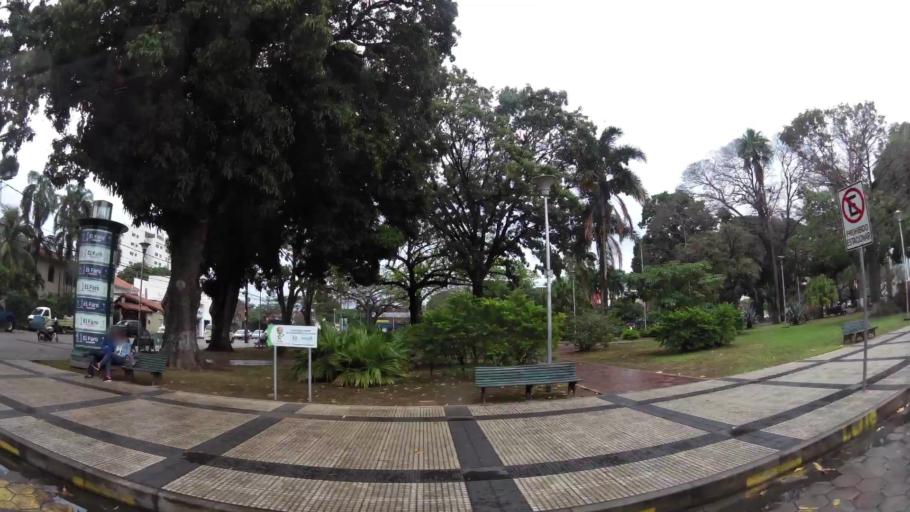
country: BO
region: Santa Cruz
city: Santa Cruz de la Sierra
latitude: -17.7944
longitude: -63.1802
